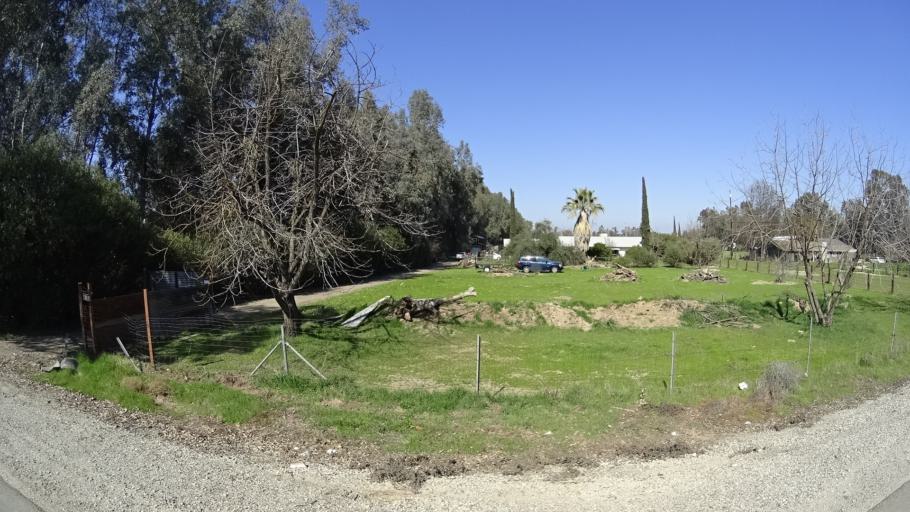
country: US
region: California
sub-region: Fresno County
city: Clovis
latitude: 36.9118
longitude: -119.7425
